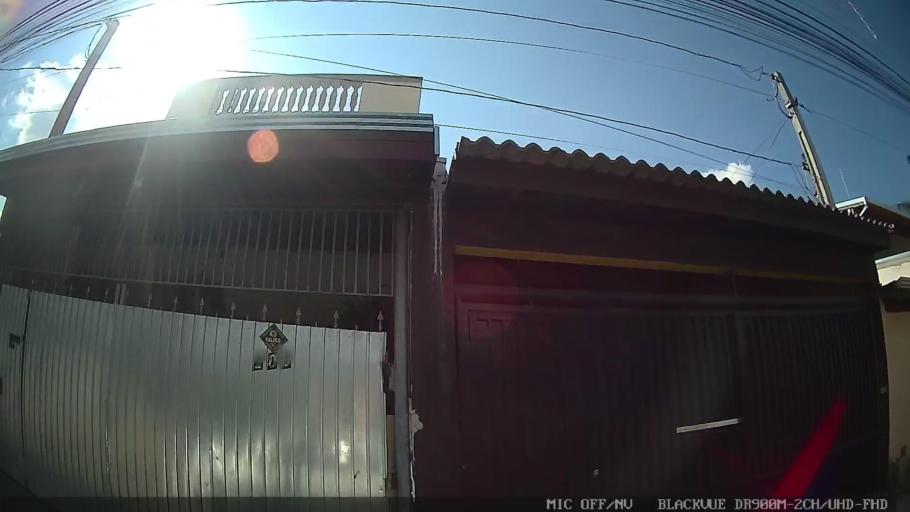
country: BR
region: Sao Paulo
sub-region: Itupeva
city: Itupeva
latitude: -23.2423
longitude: -47.0639
